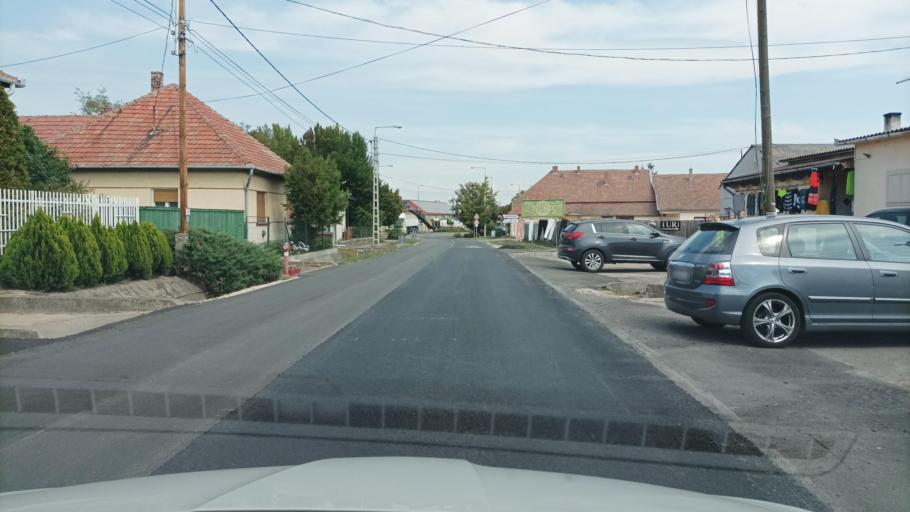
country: HU
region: Pest
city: Tura
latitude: 47.6091
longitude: 19.6006
